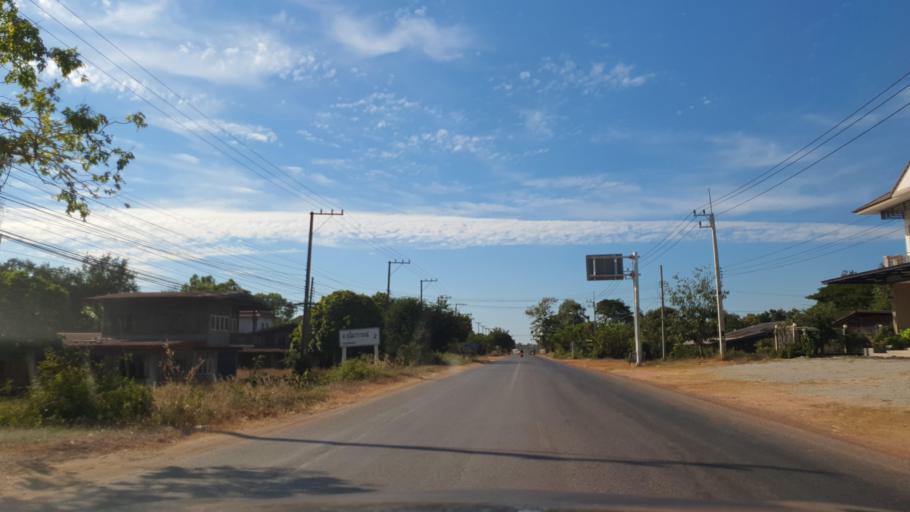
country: TH
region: Kalasin
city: Kuchinarai
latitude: 16.5347
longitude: 104.0711
